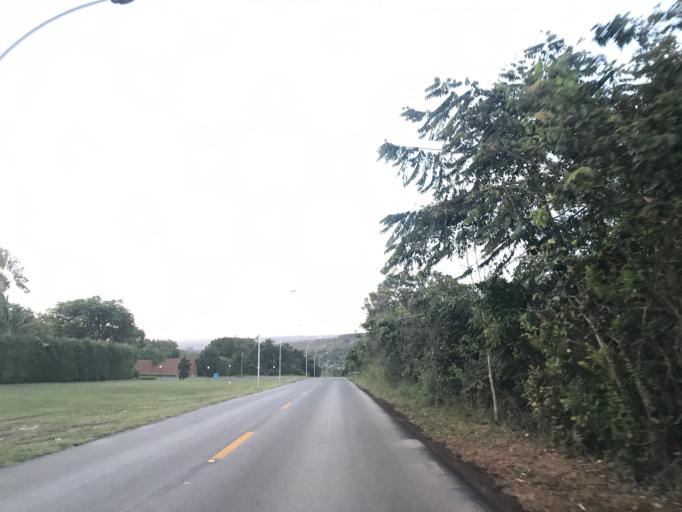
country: BR
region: Federal District
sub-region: Brasilia
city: Brasilia
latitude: -15.8013
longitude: -47.8020
